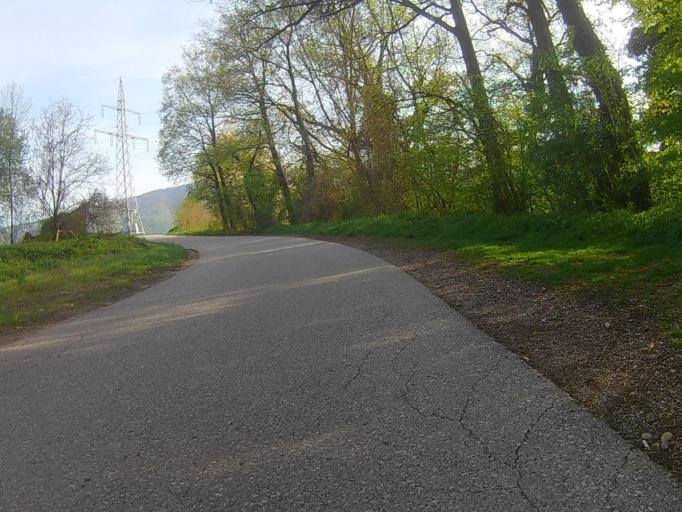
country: SI
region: Maribor
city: Limbus
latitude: 46.5612
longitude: 15.5858
